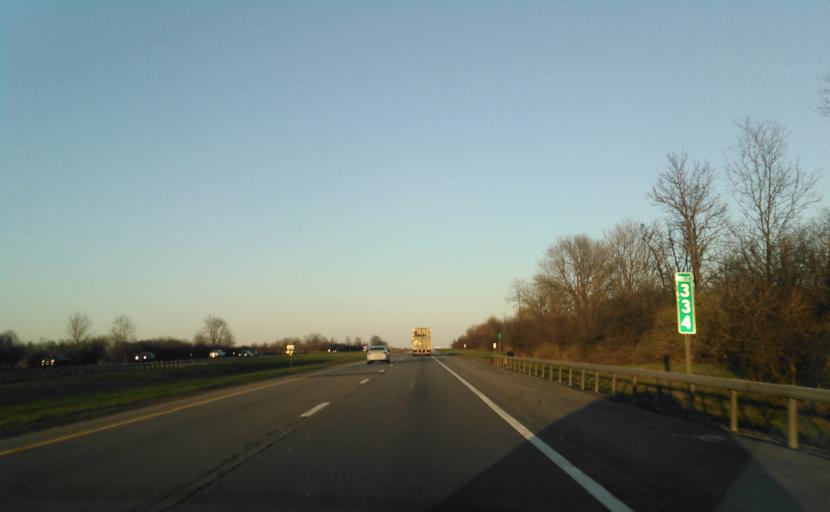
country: US
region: New York
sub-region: Ontario County
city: Clifton Springs
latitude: 42.9739
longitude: -77.1124
